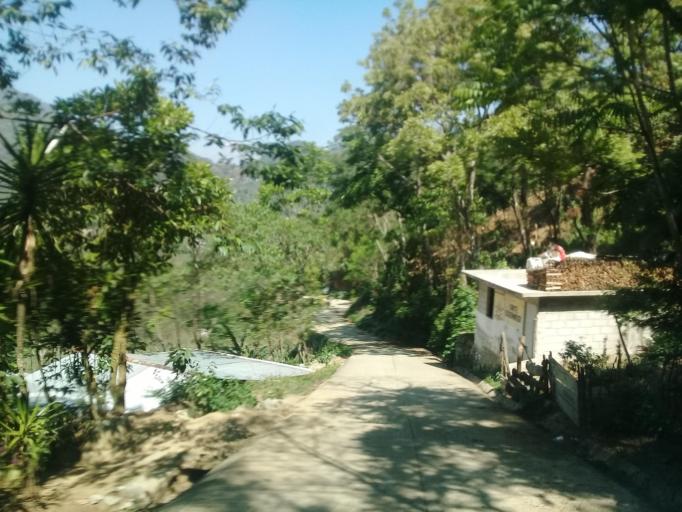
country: MX
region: Veracruz
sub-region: Tlilapan
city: Tonalixco
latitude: 18.7576
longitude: -97.0393
